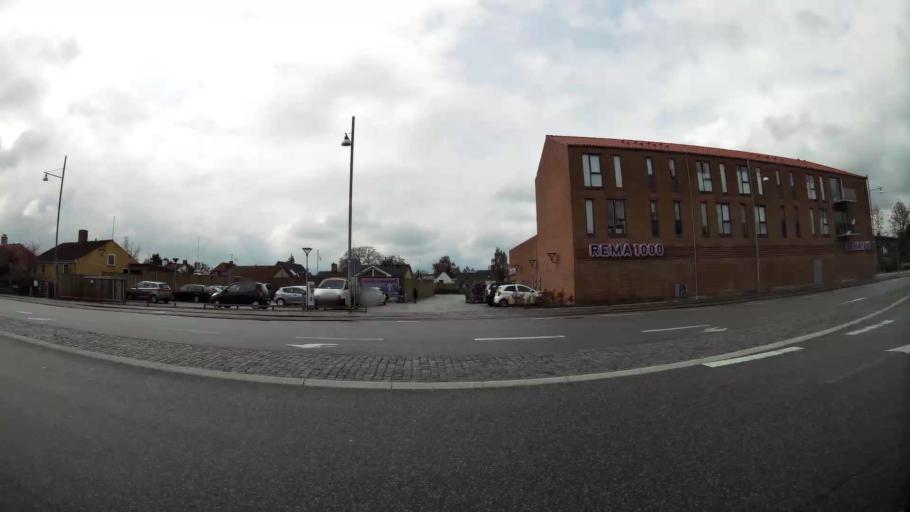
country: DK
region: Capital Region
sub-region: Glostrup Kommune
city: Glostrup
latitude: 55.6613
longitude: 12.4031
